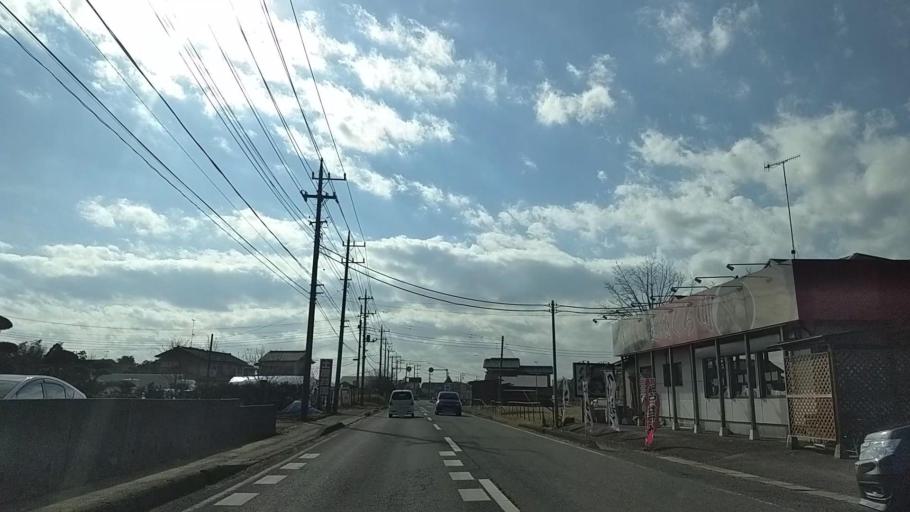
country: JP
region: Chiba
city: Naruto
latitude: 35.6474
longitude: 140.4647
